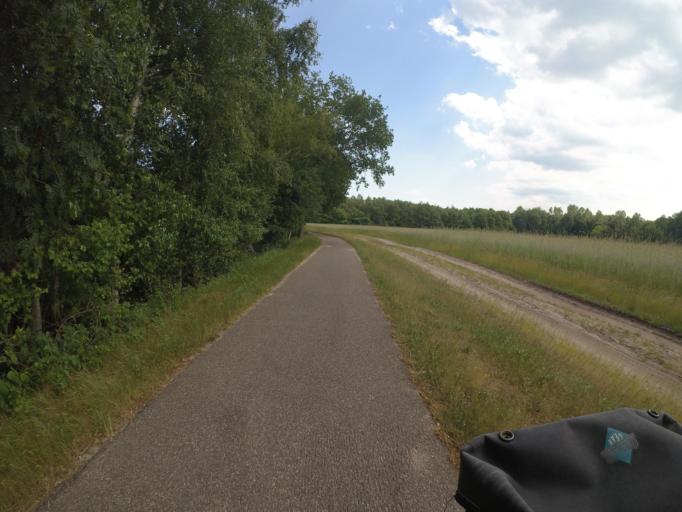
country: NL
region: Drenthe
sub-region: Gemeente Westerveld
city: Dwingeloo
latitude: 52.9080
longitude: 6.4684
